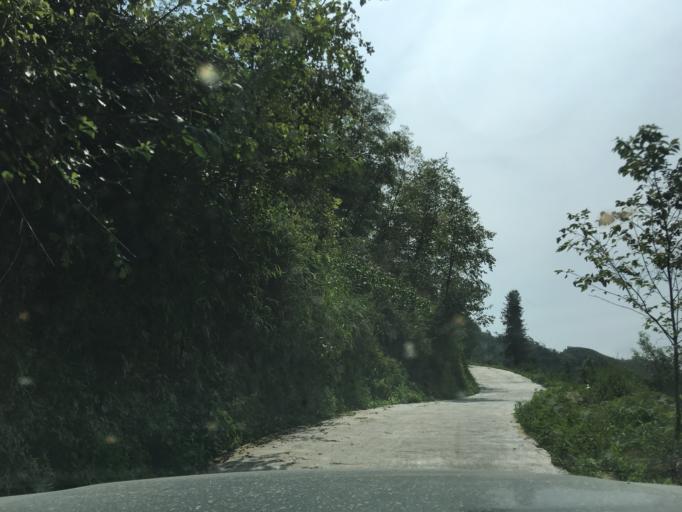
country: CN
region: Guangxi Zhuangzu Zizhiqu
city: Xinzhou
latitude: 24.9693
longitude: 105.6197
